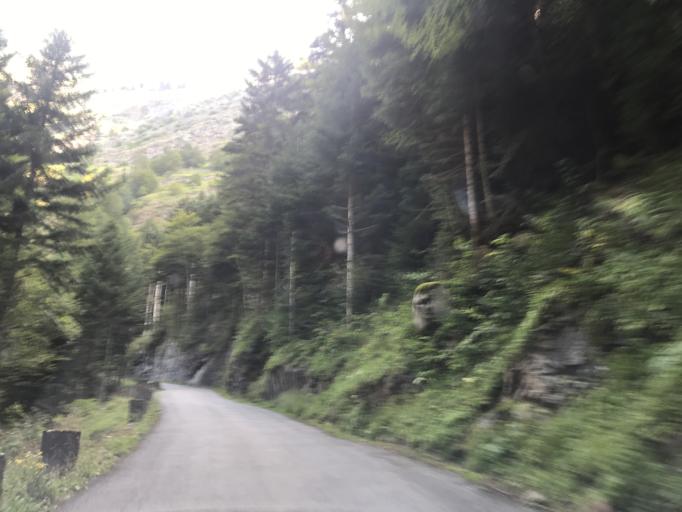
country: FR
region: Midi-Pyrenees
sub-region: Departement des Hautes-Pyrenees
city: Saint-Lary-Soulan
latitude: 42.8103
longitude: 0.2213
